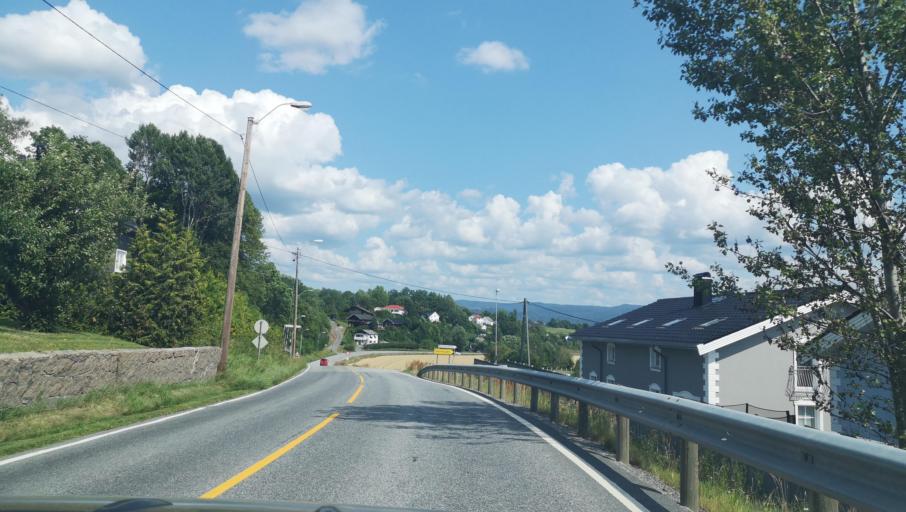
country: NO
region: Buskerud
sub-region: Ovre Eiker
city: Hokksund
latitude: 59.7333
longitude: 9.8488
